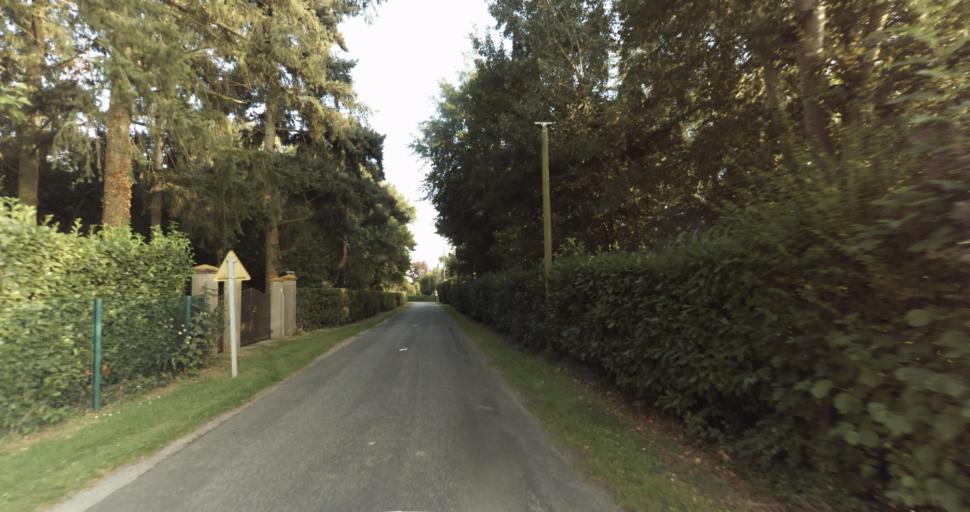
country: FR
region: Haute-Normandie
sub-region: Departement de l'Eure
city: Marcilly-sur-Eure
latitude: 48.8386
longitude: 1.2806
